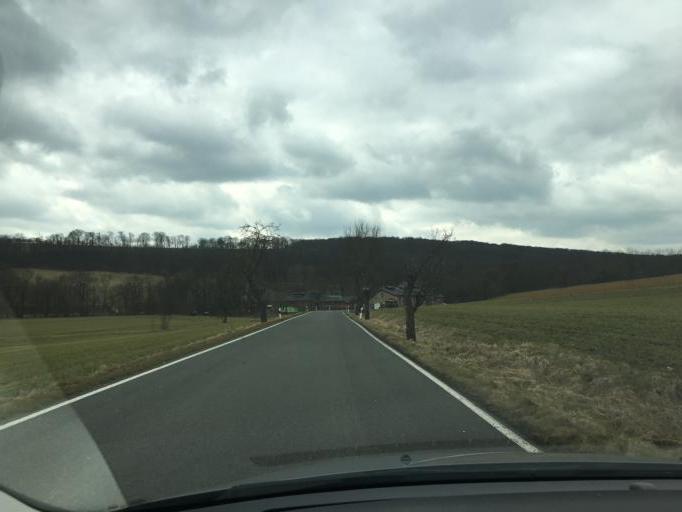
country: DE
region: Thuringia
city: Kiliansroda
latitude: 50.9237
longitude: 11.3732
